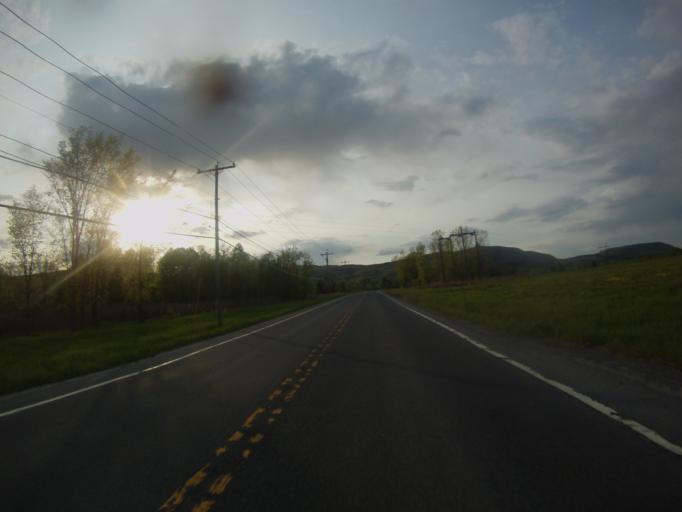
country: US
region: New York
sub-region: Essex County
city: Ticonderoga
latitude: 43.8677
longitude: -73.4392
